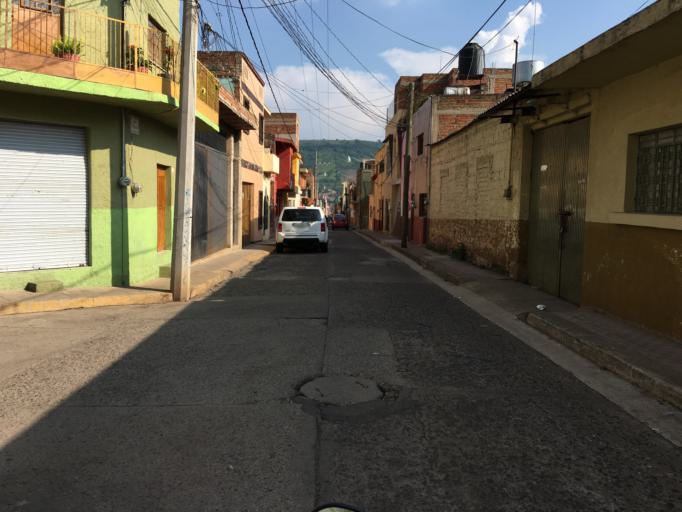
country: MX
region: Jalisco
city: Atotonilco el Alto
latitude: 20.5542
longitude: -102.5072
